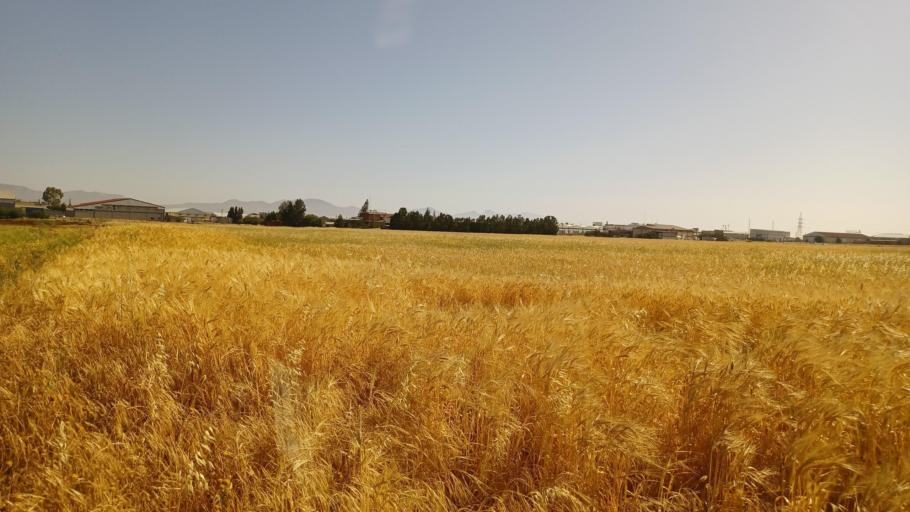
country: CY
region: Lefkosia
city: Kokkinotrimithia
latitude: 35.1457
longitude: 33.2205
